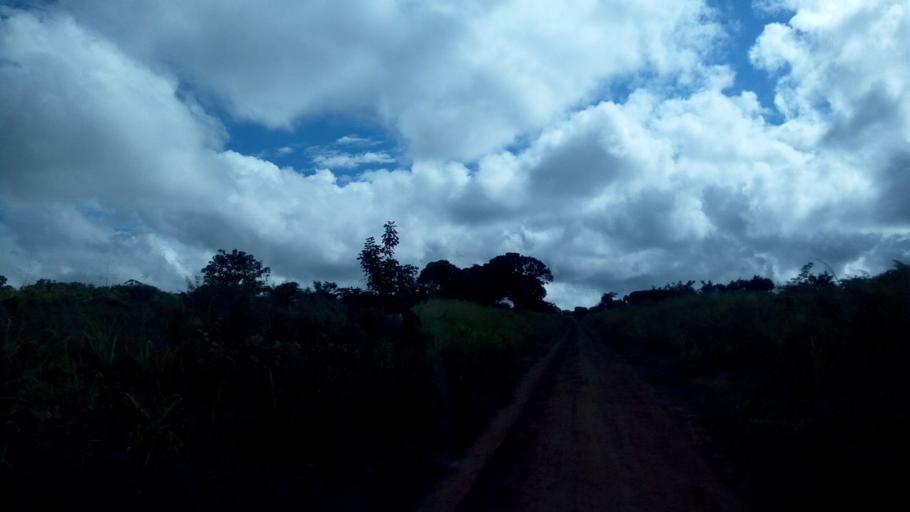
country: ZM
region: Northern
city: Kaputa
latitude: -8.3925
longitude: 28.9449
